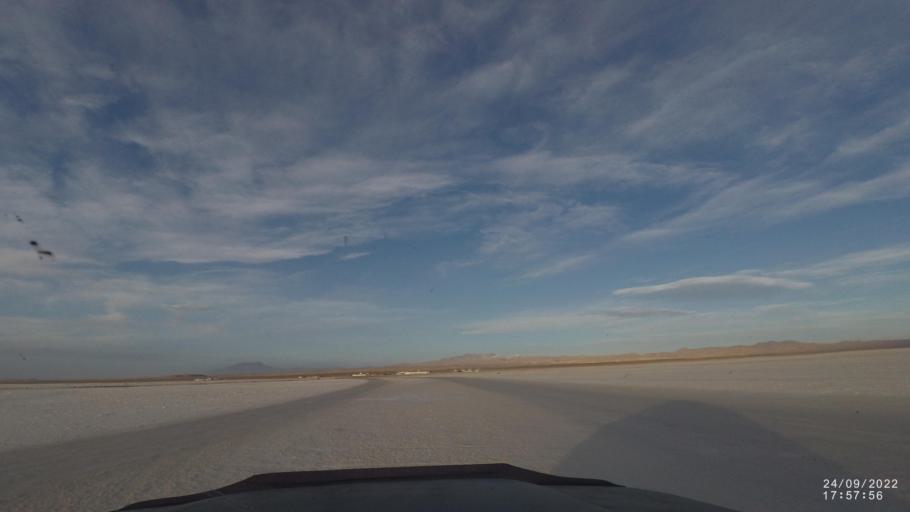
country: BO
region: Potosi
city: Colchani
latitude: -20.3180
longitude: -66.9837
